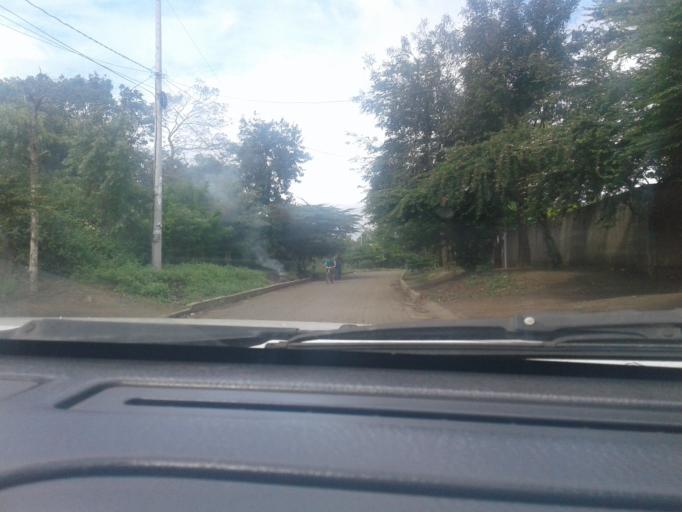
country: NI
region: Carazo
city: San Marcos
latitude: 11.8978
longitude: -86.1761
